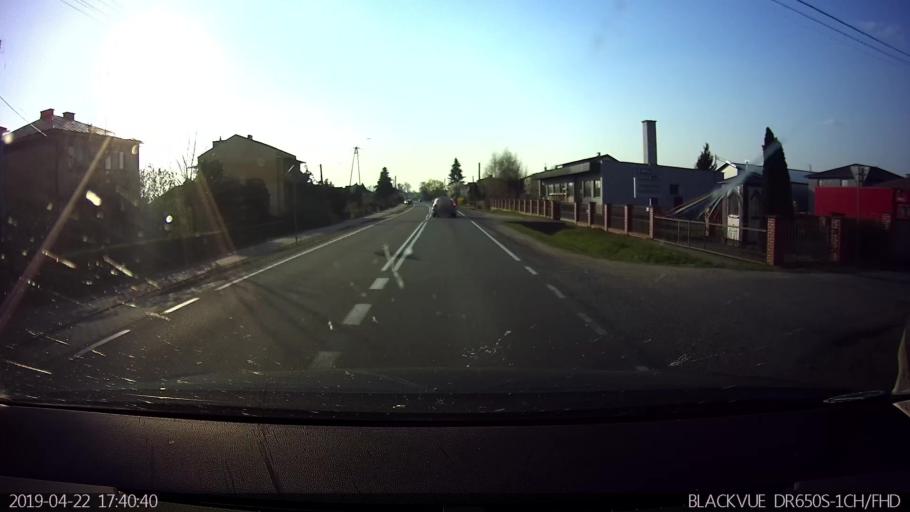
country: PL
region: Masovian Voivodeship
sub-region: Powiat wegrowski
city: Miedzna
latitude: 52.3995
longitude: 22.1220
